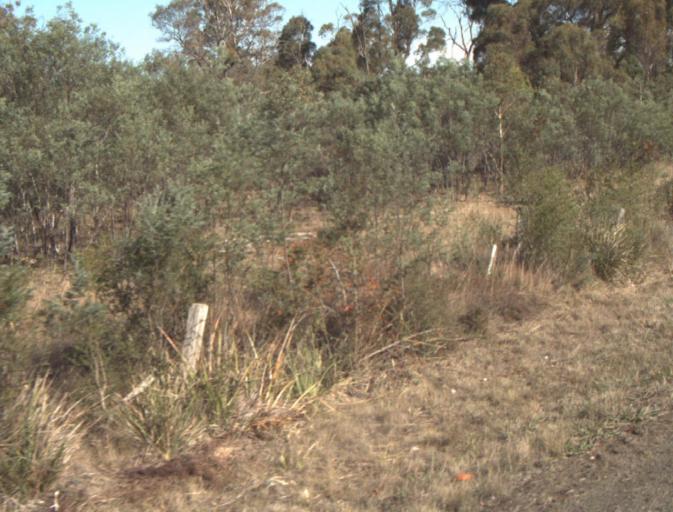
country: AU
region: Tasmania
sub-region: Launceston
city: Mayfield
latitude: -41.3654
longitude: 147.1442
